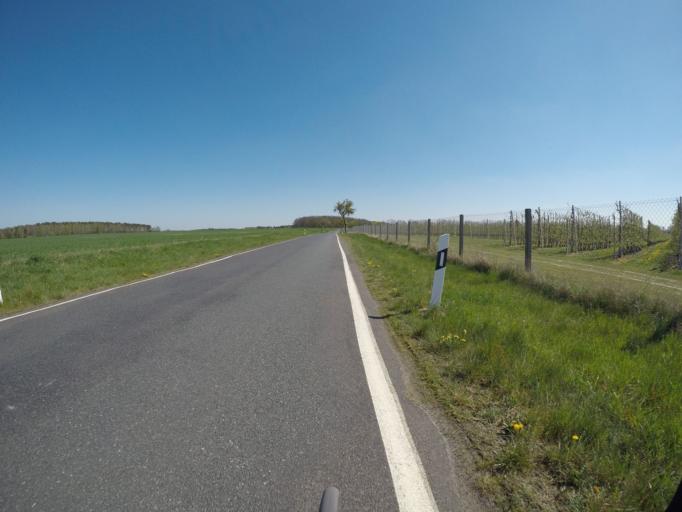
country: DE
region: Brandenburg
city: Werftpfuhl
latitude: 52.6314
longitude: 13.8107
